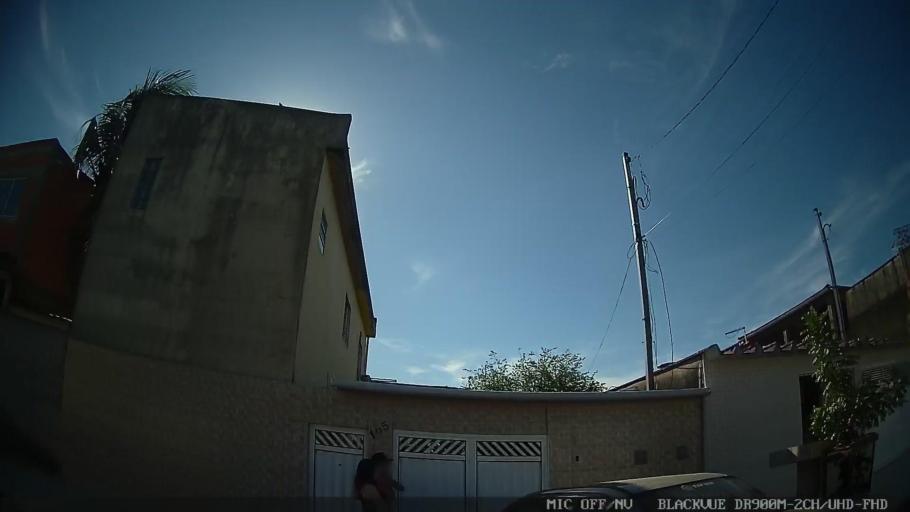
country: BR
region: Sao Paulo
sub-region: Santos
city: Santos
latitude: -23.9353
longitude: -46.2876
